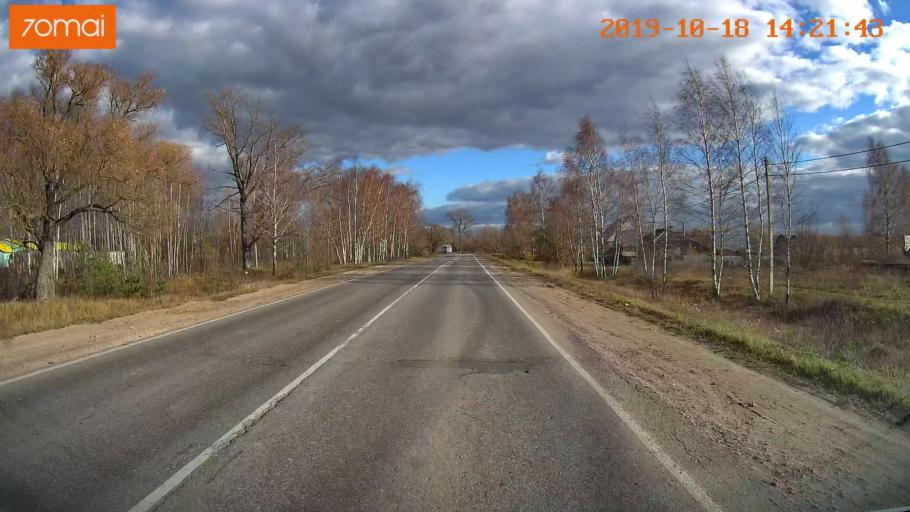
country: RU
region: Rjazan
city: Tuma
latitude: 55.1465
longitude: 40.4624
